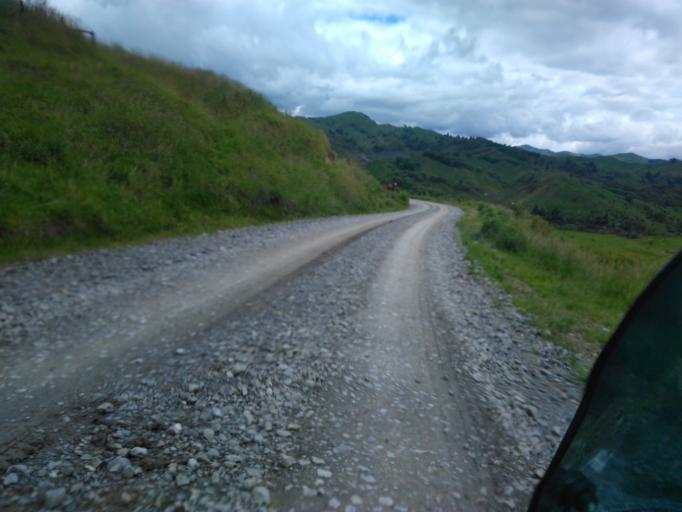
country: NZ
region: Gisborne
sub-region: Gisborne District
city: Gisborne
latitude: -38.0804
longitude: 178.0672
